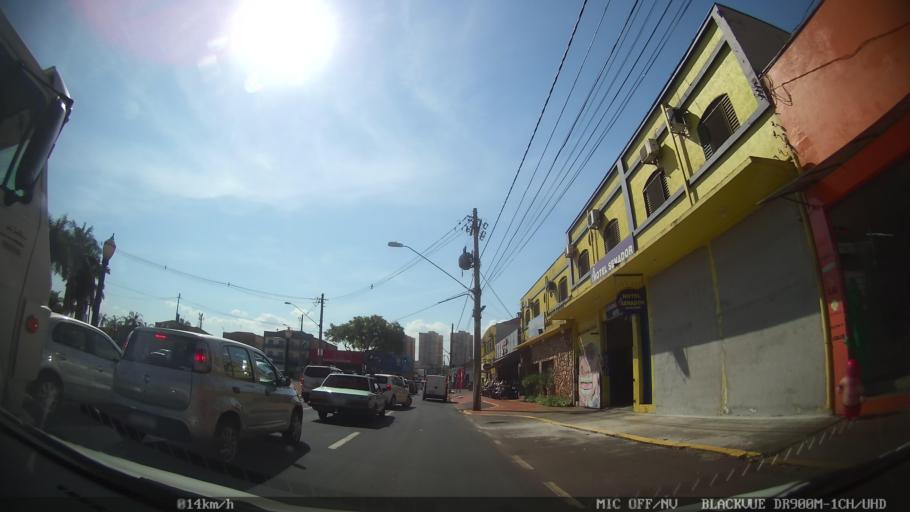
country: BR
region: Sao Paulo
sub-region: Ribeirao Preto
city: Ribeirao Preto
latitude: -21.1700
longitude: -47.8114
